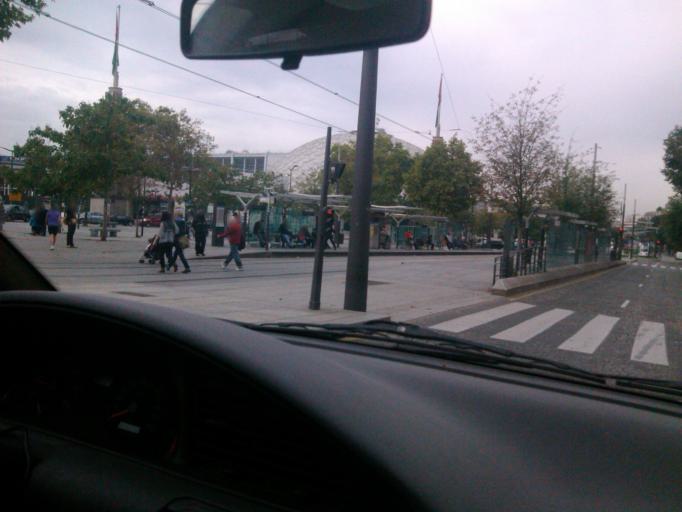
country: FR
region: Ile-de-France
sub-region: Departement des Hauts-de-Seine
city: Vanves
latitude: 48.8299
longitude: 2.2962
